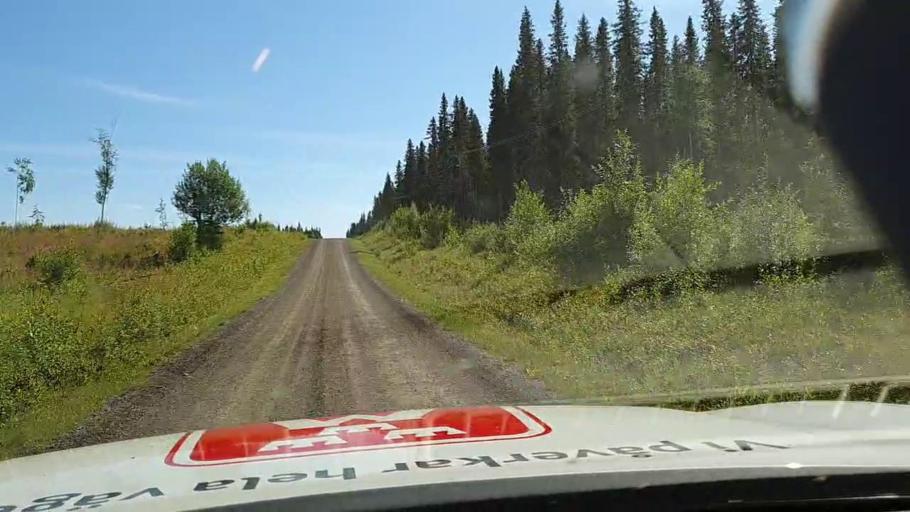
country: SE
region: Jaemtland
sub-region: Stroemsunds Kommun
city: Stroemsund
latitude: 63.7850
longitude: 15.3033
